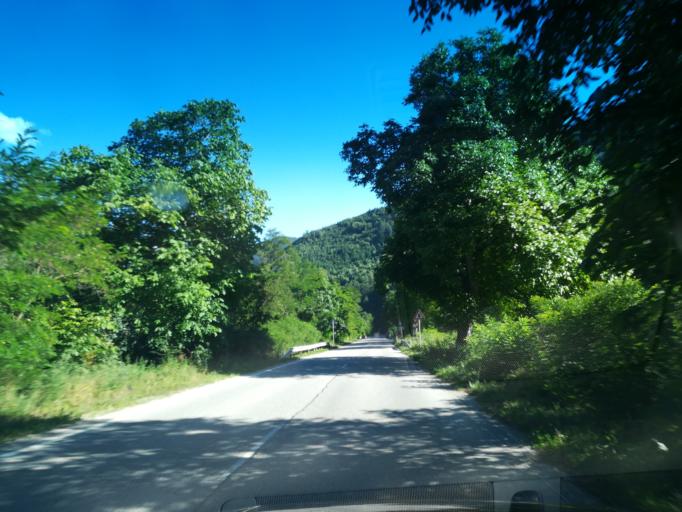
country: BG
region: Smolyan
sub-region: Obshtina Chepelare
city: Chepelare
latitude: 41.8405
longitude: 24.6795
